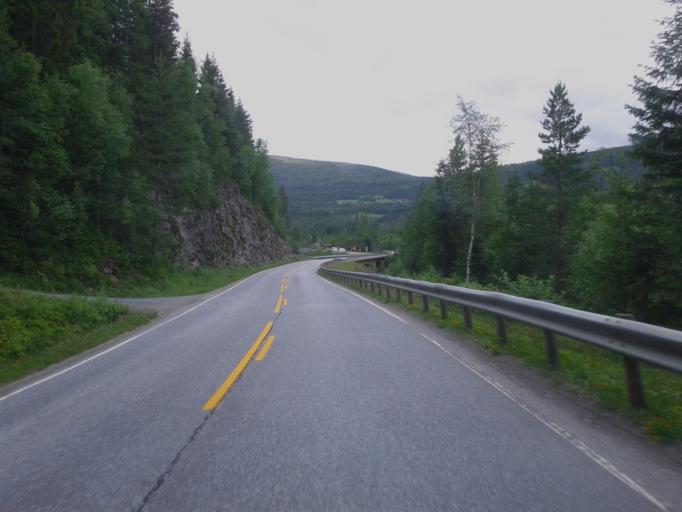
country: NO
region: Sor-Trondelag
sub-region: Holtalen
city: Alen
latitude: 62.8622
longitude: 11.2124
